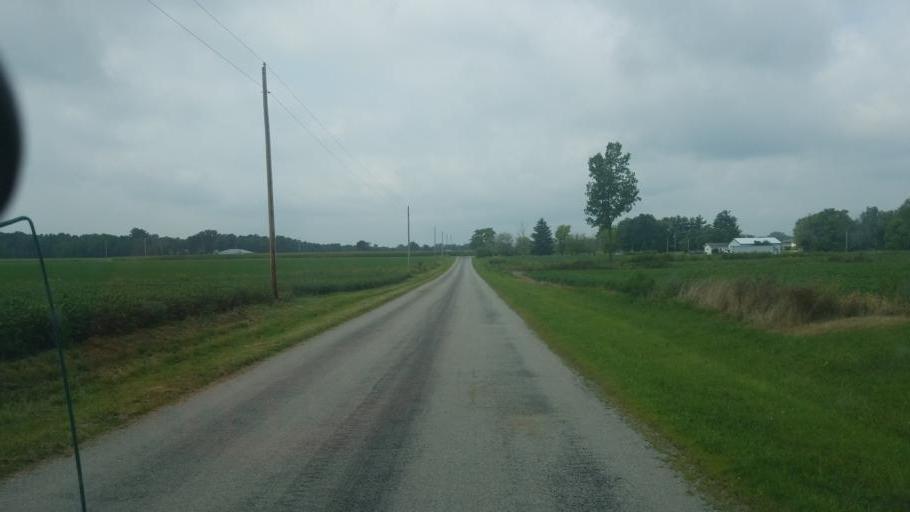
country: US
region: Ohio
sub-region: Huron County
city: Greenwich
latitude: 41.0108
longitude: -82.5059
